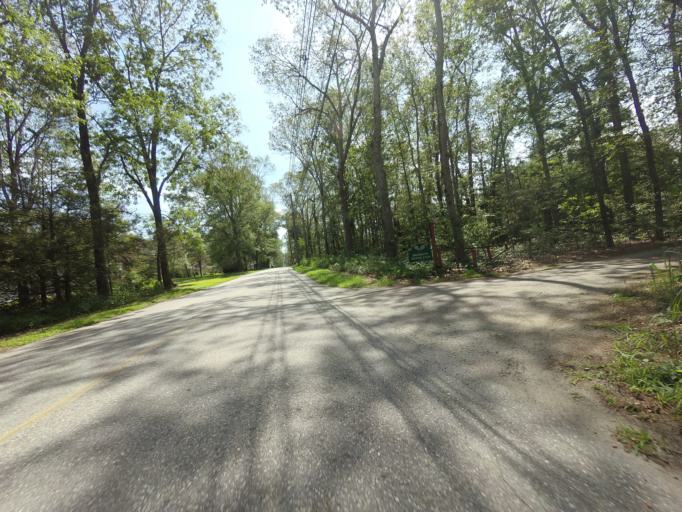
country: US
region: Connecticut
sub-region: Windham County
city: East Brooklyn
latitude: 41.8160
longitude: -71.9234
